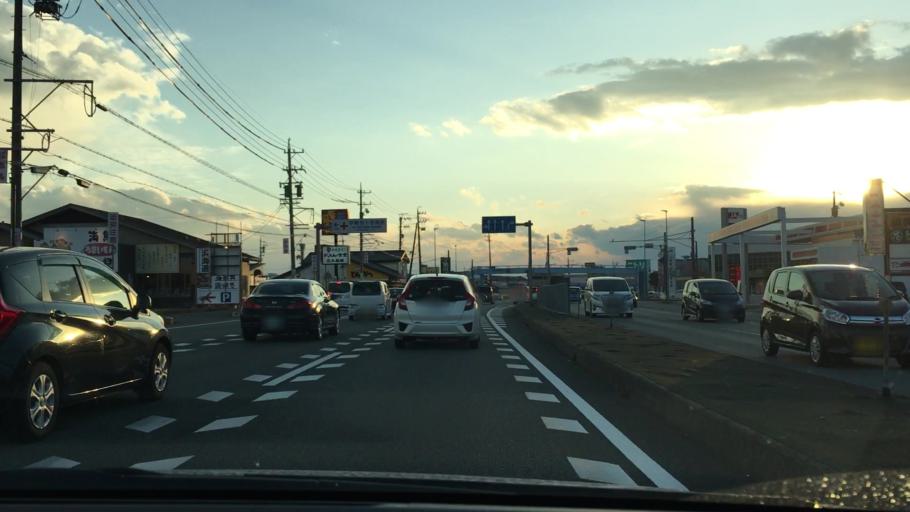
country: JP
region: Mie
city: Ise
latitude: 34.5070
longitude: 136.7104
